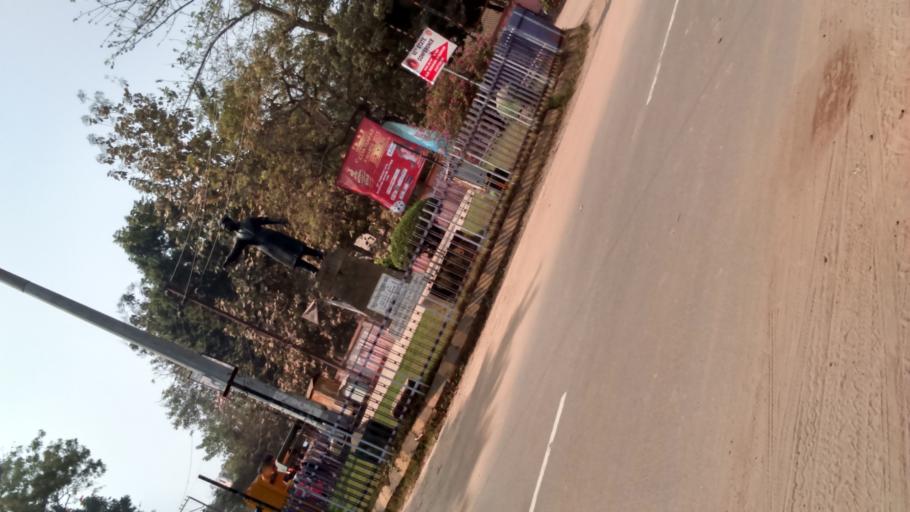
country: IN
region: Odisha
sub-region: Cuttack
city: Cuttack
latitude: 20.4818
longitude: 85.8726
